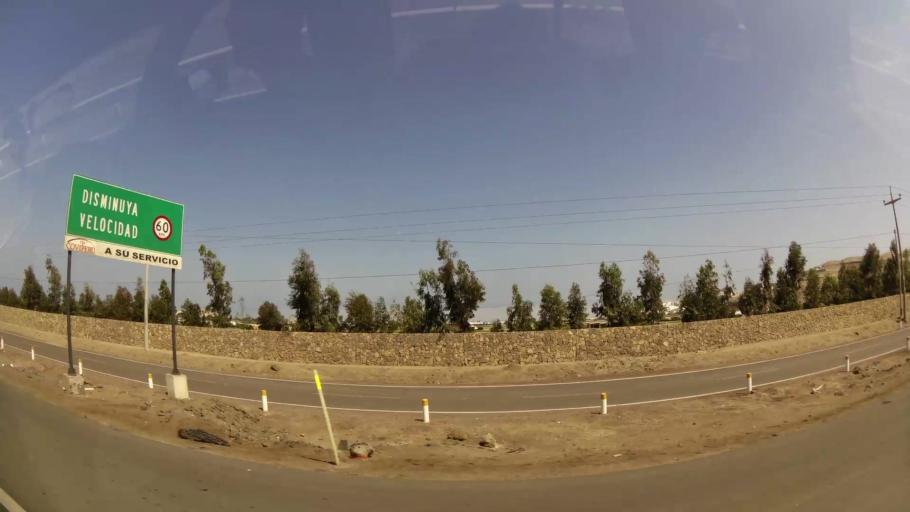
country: PE
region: Lima
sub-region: Provincia de Canete
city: Asia
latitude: -12.7486
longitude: -76.6099
